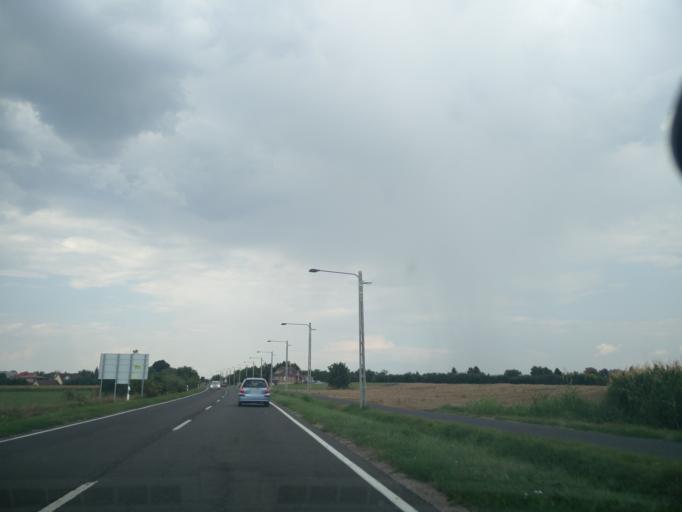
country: HU
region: Fejer
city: Polgardi
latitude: 47.0546
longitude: 18.3054
